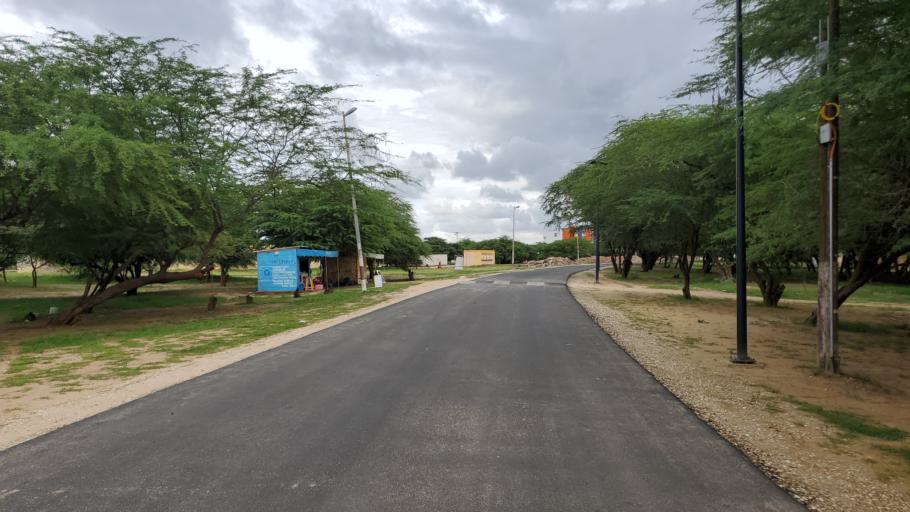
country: SN
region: Saint-Louis
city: Saint-Louis
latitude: 16.0672
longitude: -16.4232
